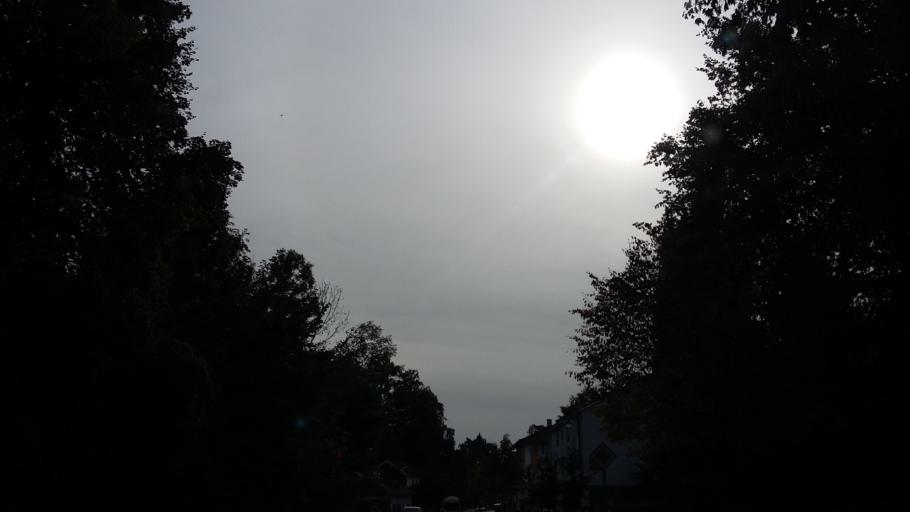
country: DE
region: Bavaria
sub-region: Upper Bavaria
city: Berg
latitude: 47.9687
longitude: 11.3578
